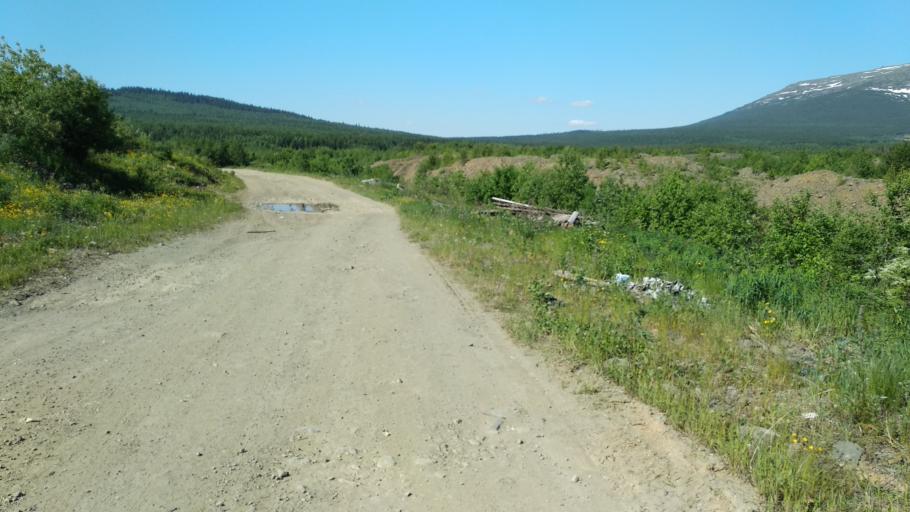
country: RU
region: Sverdlovsk
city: Valerianovsk
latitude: 59.4992
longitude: 59.1889
